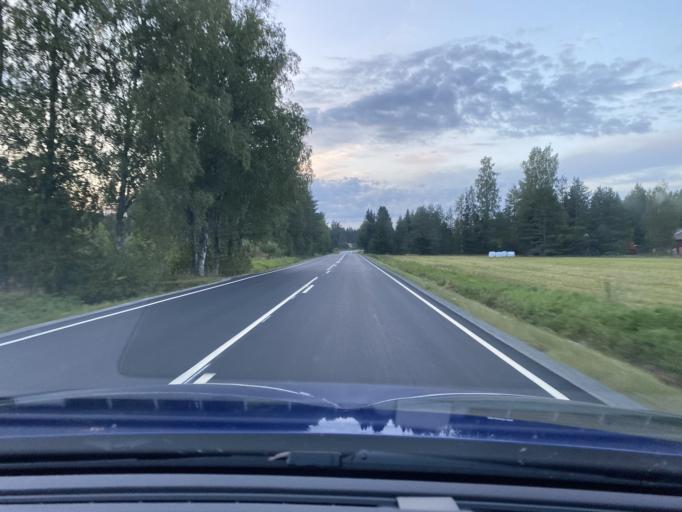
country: FI
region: Satakunta
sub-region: Pohjois-Satakunta
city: Honkajoki
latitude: 62.0718
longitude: 22.2497
